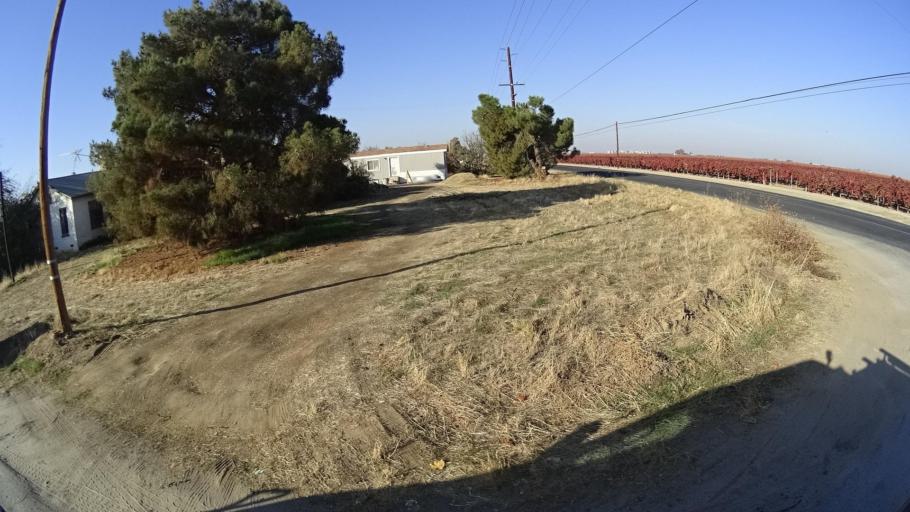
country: US
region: California
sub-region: Tulare County
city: Richgrove
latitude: 35.7758
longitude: -119.1697
